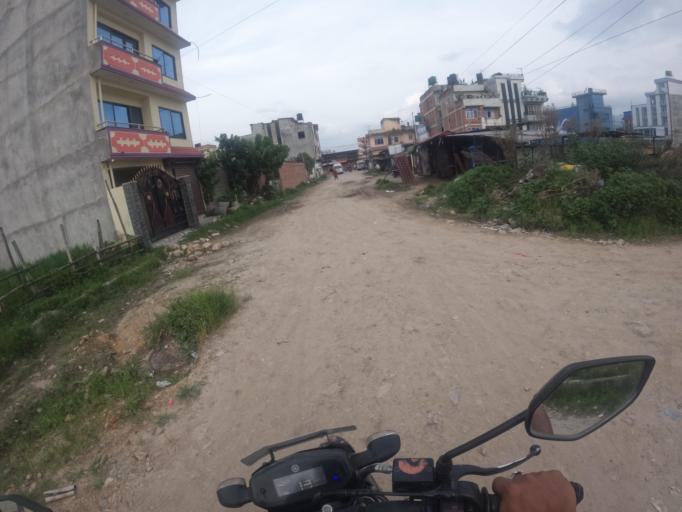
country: NP
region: Central Region
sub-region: Bagmati Zone
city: Bhaktapur
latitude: 27.6793
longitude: 85.3978
